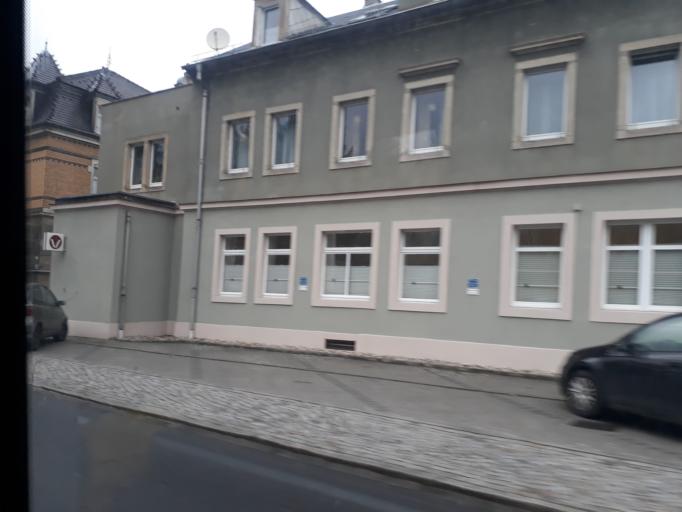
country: DE
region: Saxony
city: Dohna
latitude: 50.9876
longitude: 13.8049
